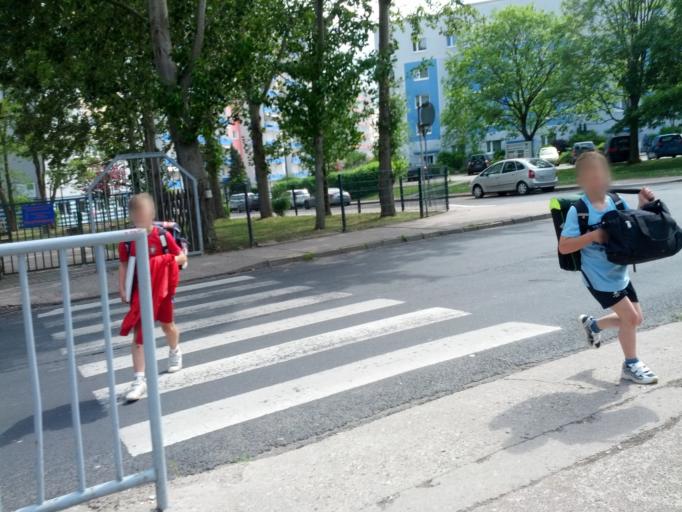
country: DE
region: Thuringia
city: Eisenach
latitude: 50.9966
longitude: 10.3090
